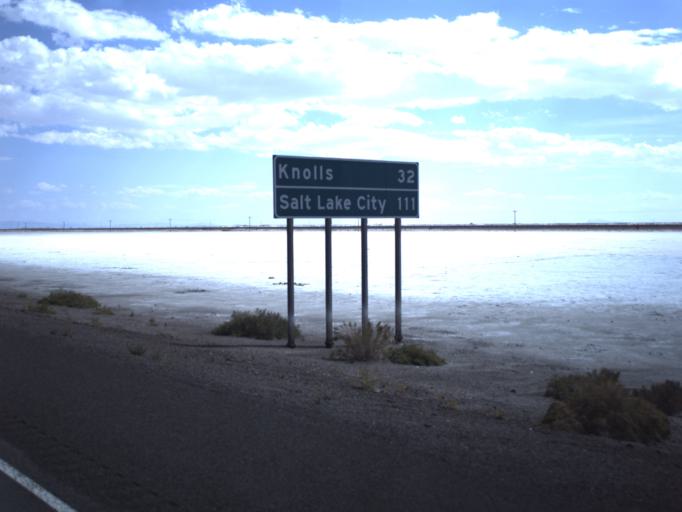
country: US
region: Utah
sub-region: Tooele County
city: Wendover
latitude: 40.7382
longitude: -113.8395
